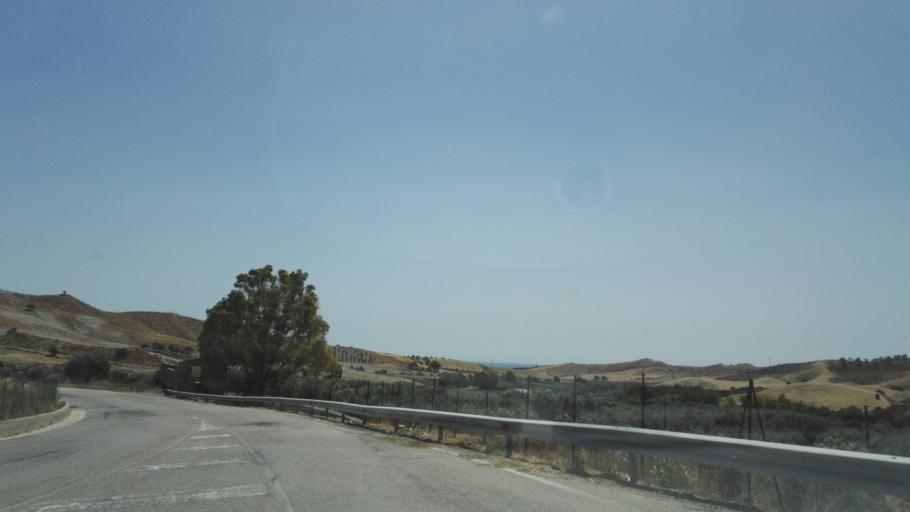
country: IT
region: Calabria
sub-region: Provincia di Catanzaro
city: Guardavalle
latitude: 38.4899
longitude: 16.5368
